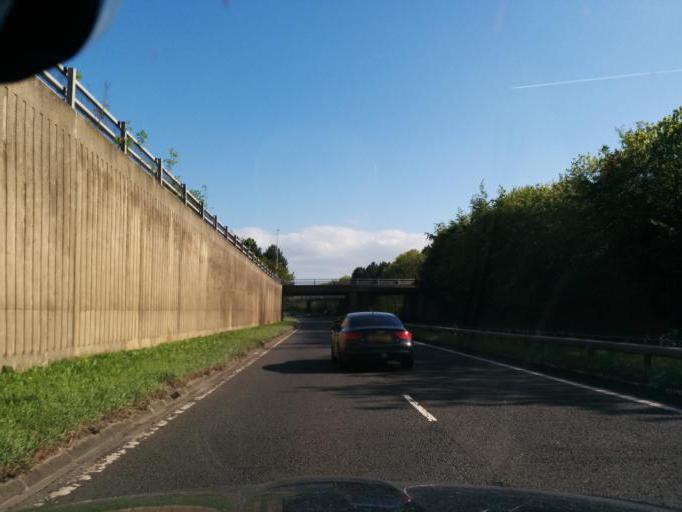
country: GB
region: England
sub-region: Northumberland
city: Bedlington
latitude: 55.1290
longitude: -1.5576
